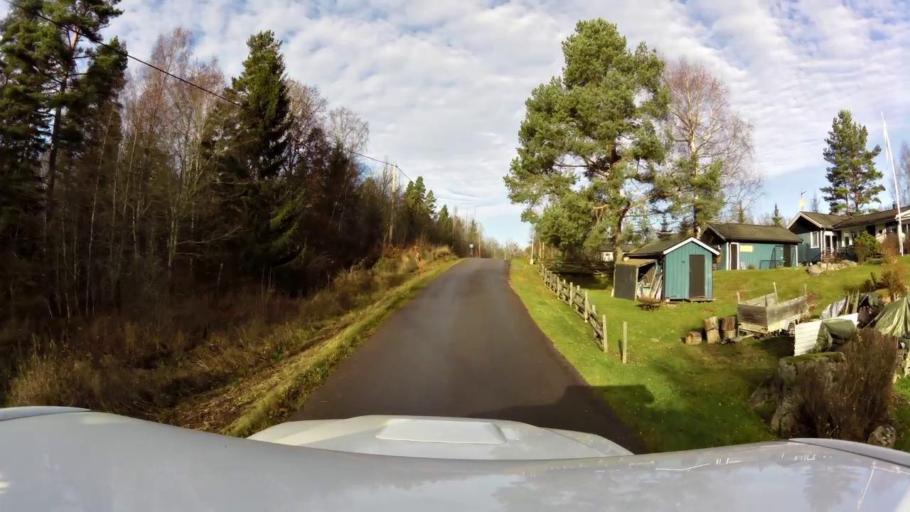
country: SE
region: OEstergoetland
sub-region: Linkopings Kommun
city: Sturefors
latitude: 58.2574
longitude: 15.6958
